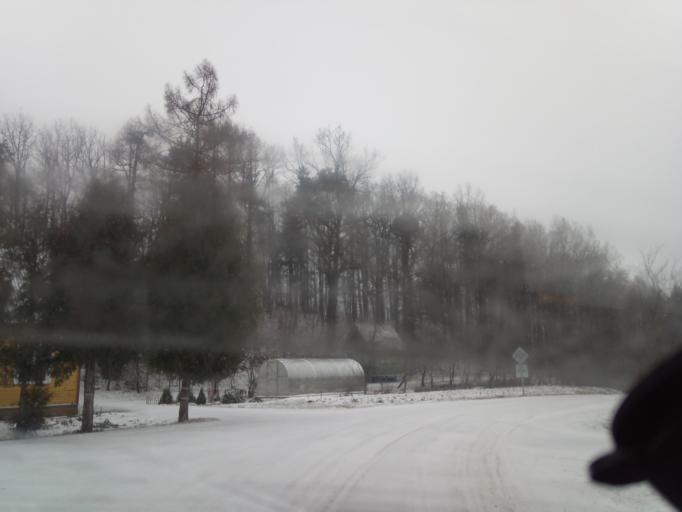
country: LT
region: Utenos apskritis
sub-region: Anyksciai
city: Anyksciai
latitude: 55.4218
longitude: 25.1093
